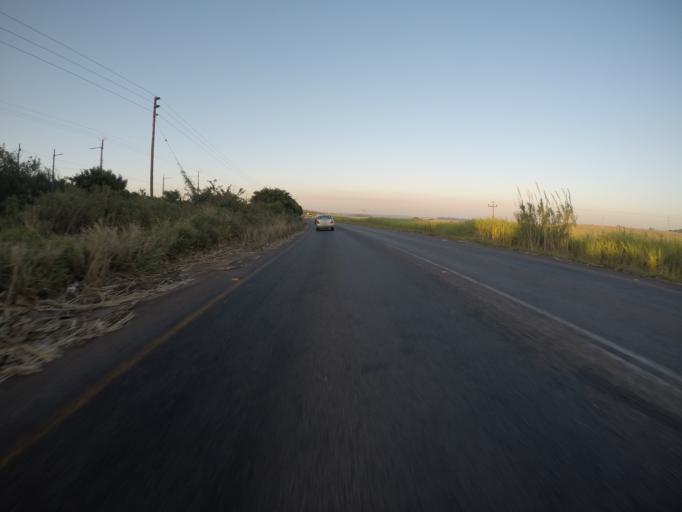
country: ZA
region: KwaZulu-Natal
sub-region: uThungulu District Municipality
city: Empangeni
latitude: -28.8063
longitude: 31.8923
